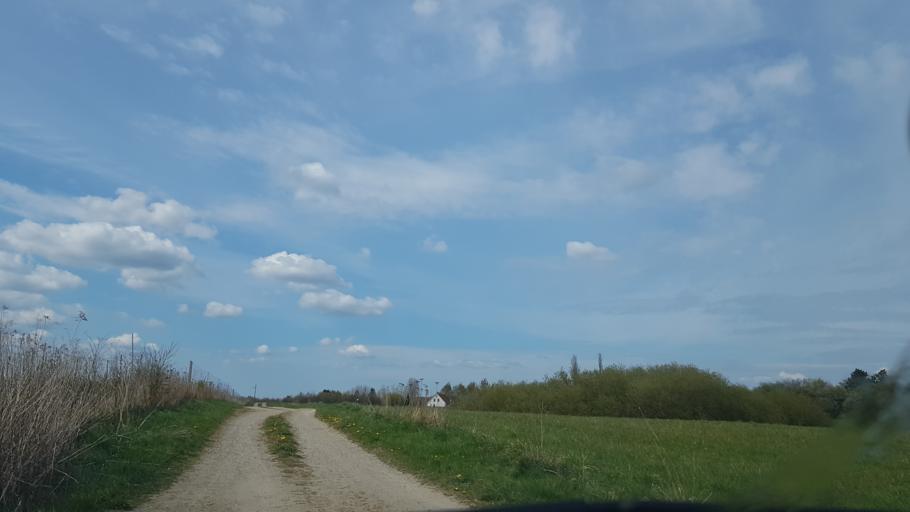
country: DK
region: Capital Region
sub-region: Allerod Kommune
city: Lillerod
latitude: 55.8968
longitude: 12.3362
